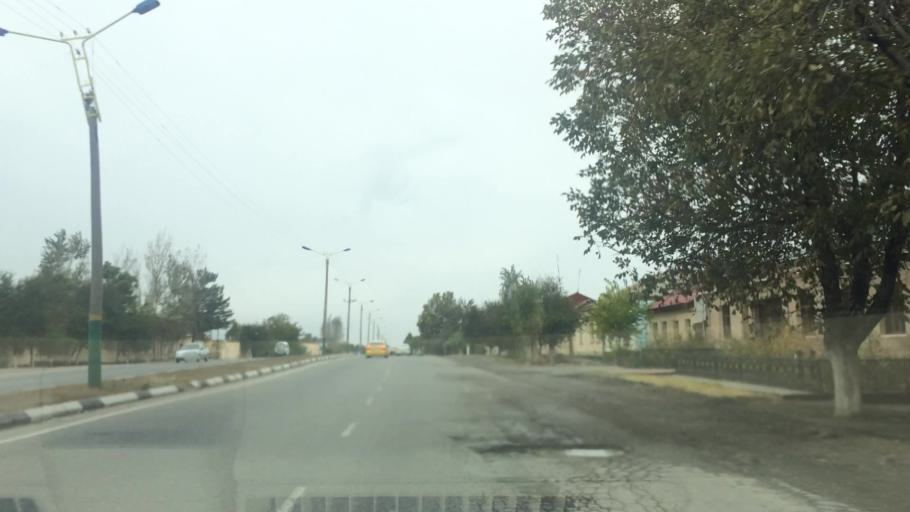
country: UZ
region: Samarqand
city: Bulung'ur
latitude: 39.7675
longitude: 67.2612
